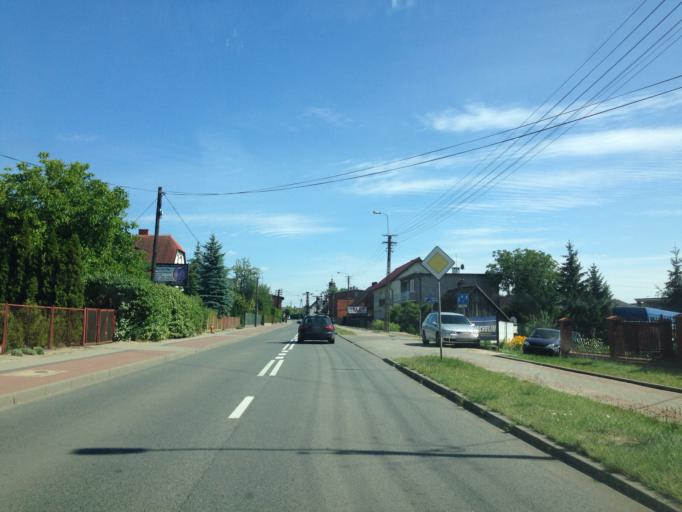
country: PL
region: Kujawsko-Pomorskie
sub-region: Powiat swiecki
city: Osie
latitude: 53.6013
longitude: 18.3389
